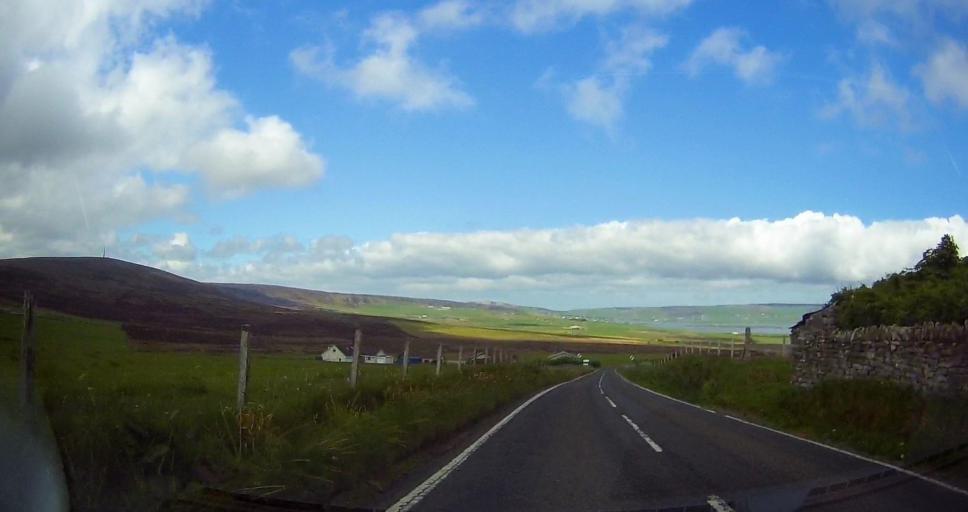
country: GB
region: Scotland
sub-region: Orkney Islands
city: Orkney
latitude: 58.9813
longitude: -3.0383
